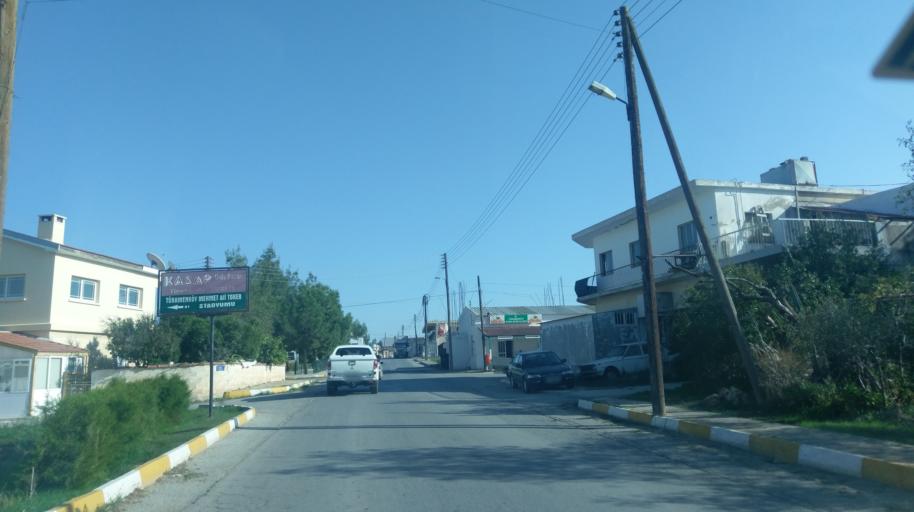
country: CY
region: Larnaka
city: Pergamos
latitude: 35.1057
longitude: 33.7150
